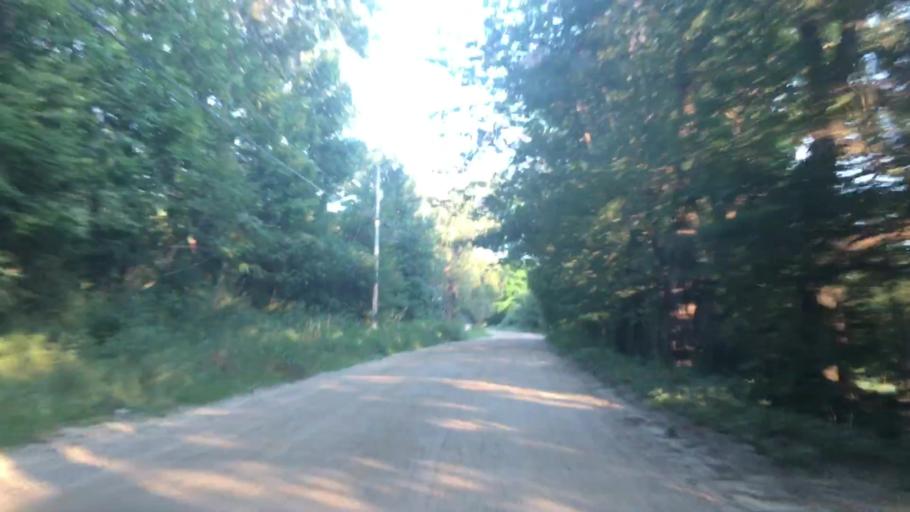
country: US
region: New Hampshire
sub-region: Belknap County
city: Barnstead
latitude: 43.4080
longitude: -71.2709
